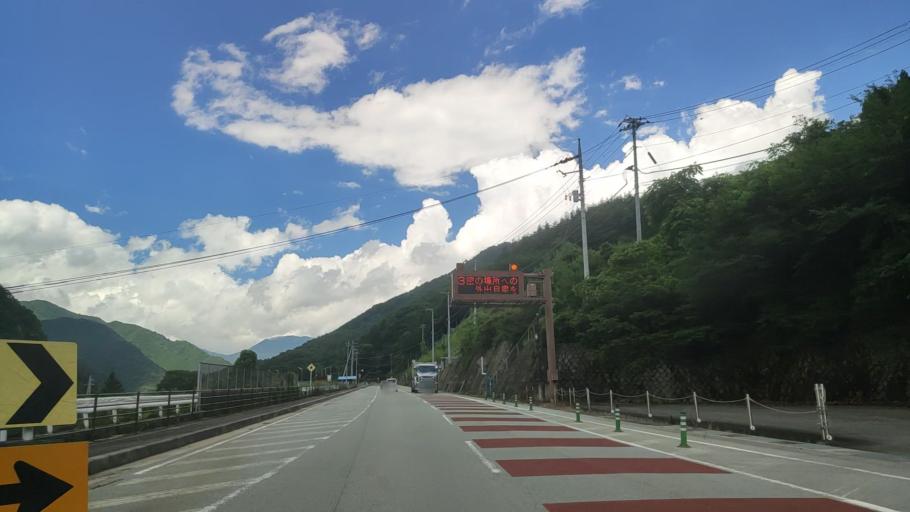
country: JP
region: Yamanashi
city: Enzan
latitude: 35.8002
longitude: 138.7481
